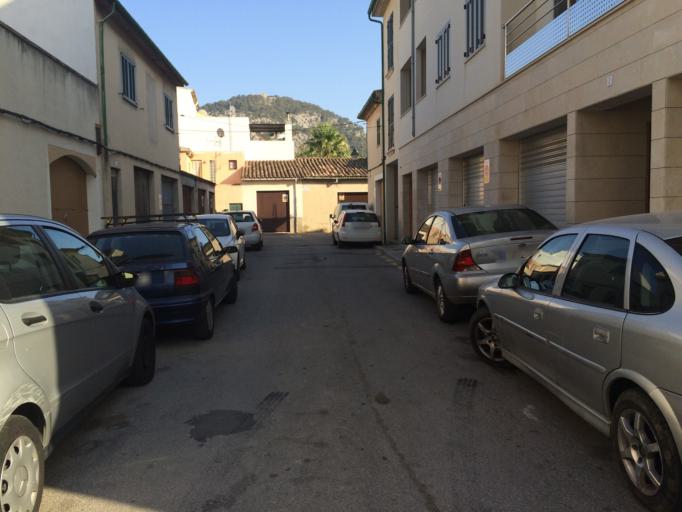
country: ES
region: Balearic Islands
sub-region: Illes Balears
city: Pollenca
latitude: 39.8806
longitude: 3.0160
